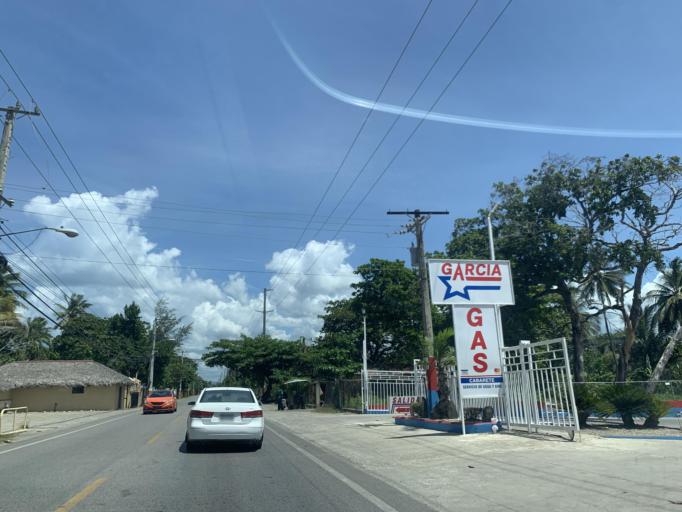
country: DO
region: Puerto Plata
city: Cabarete
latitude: 19.7437
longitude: -70.3940
